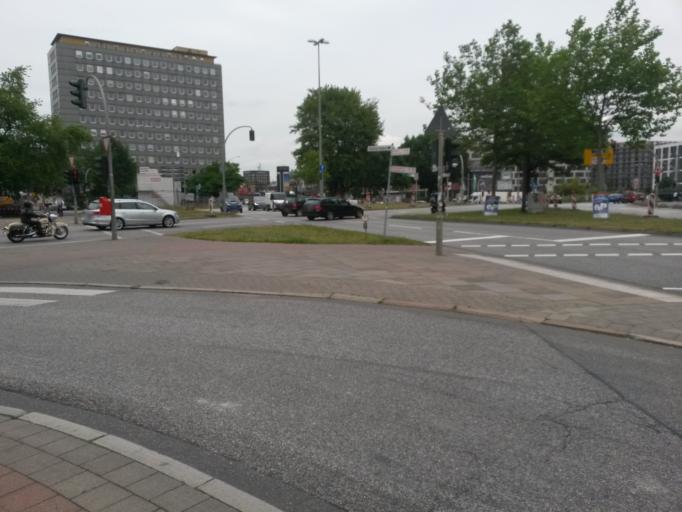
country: DE
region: Hamburg
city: Altstadt
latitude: 53.5473
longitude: 10.0051
